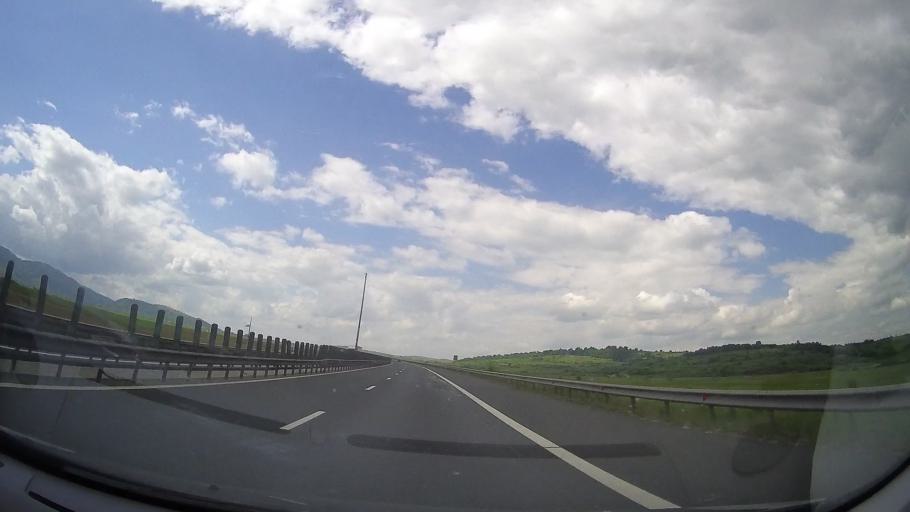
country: RO
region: Sibiu
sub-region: Comuna Orlat
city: Orlat
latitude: 45.7928
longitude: 23.9398
